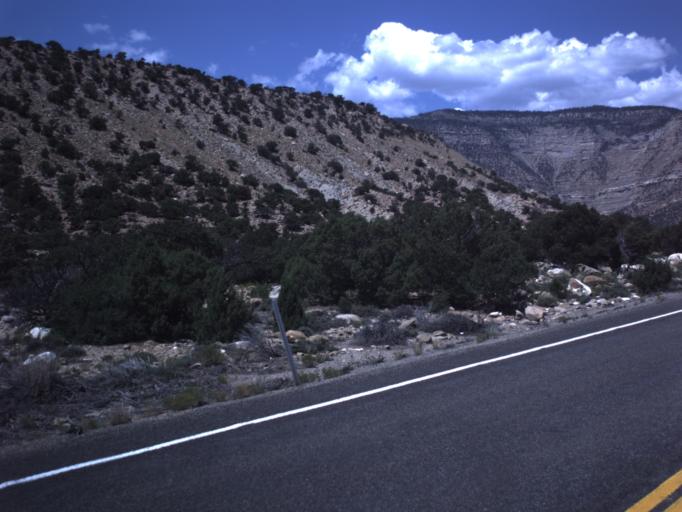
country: US
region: Utah
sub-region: Emery County
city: Orangeville
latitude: 39.2815
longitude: -111.1033
